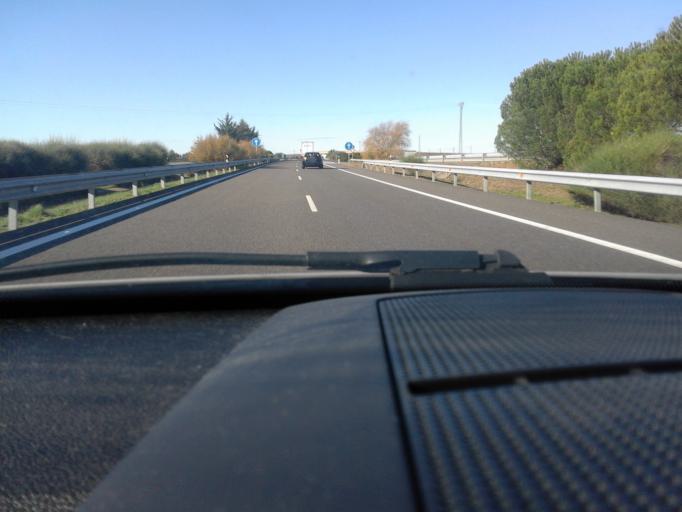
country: ES
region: Castille and Leon
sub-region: Provincia de Leon
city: Vallecillo
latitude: 42.4151
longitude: -5.2176
